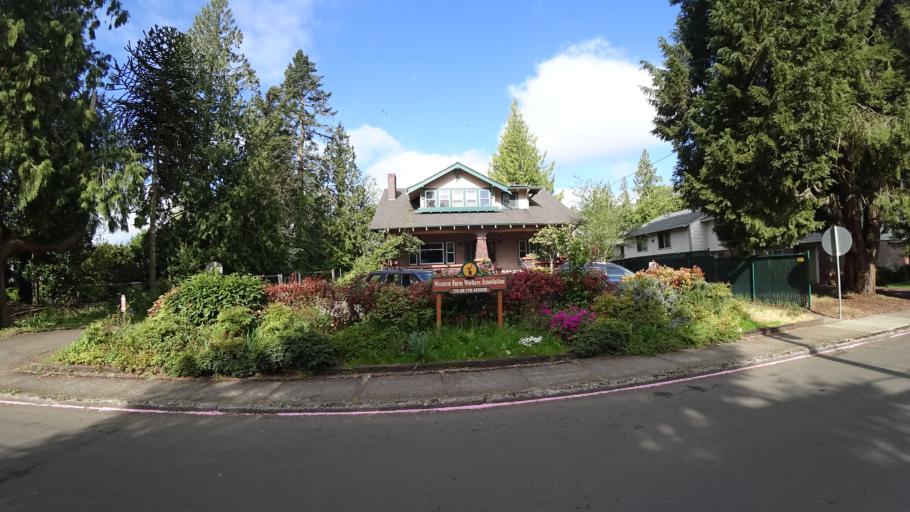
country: US
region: Oregon
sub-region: Washington County
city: Hillsboro
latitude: 45.5144
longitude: -122.9791
